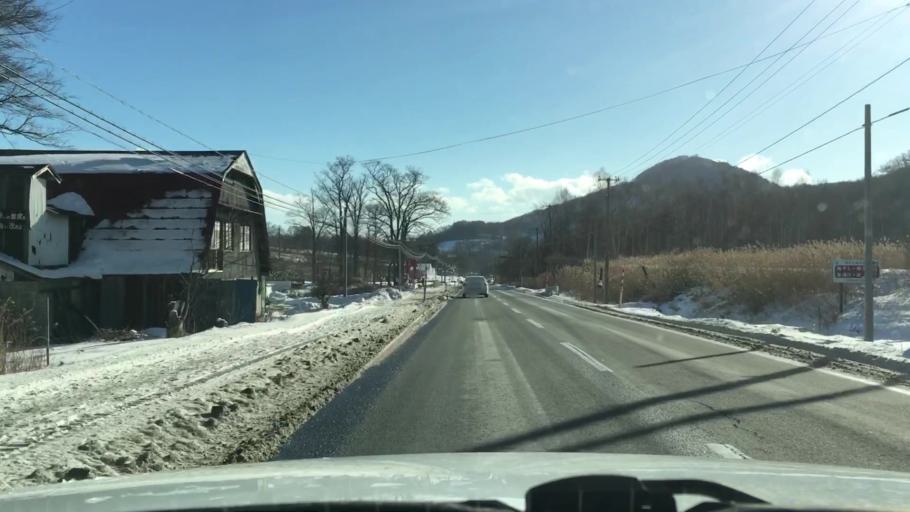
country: JP
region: Iwate
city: Morioka-shi
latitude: 39.6454
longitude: 141.3675
